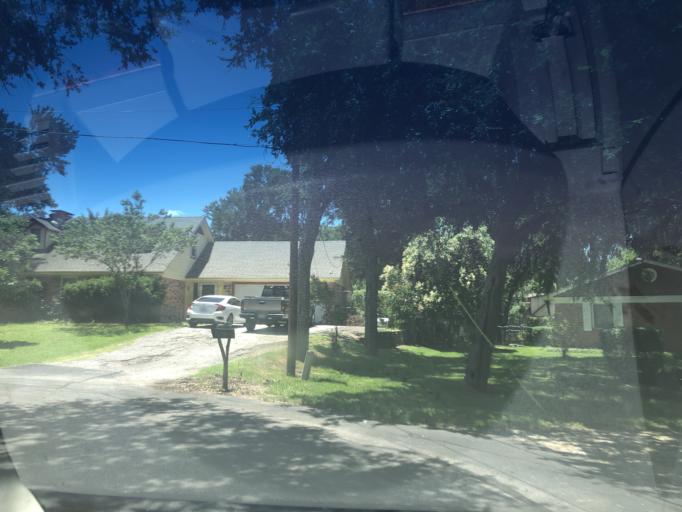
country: US
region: Texas
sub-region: Dallas County
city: Grand Prairie
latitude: 32.7744
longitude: -97.0317
